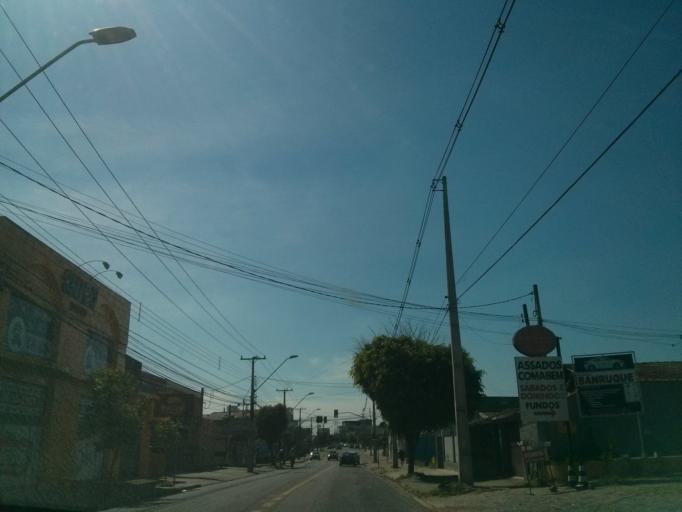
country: BR
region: Parana
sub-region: Sao Jose Dos Pinhais
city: Sao Jose dos Pinhais
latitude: -25.5461
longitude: -49.1999
